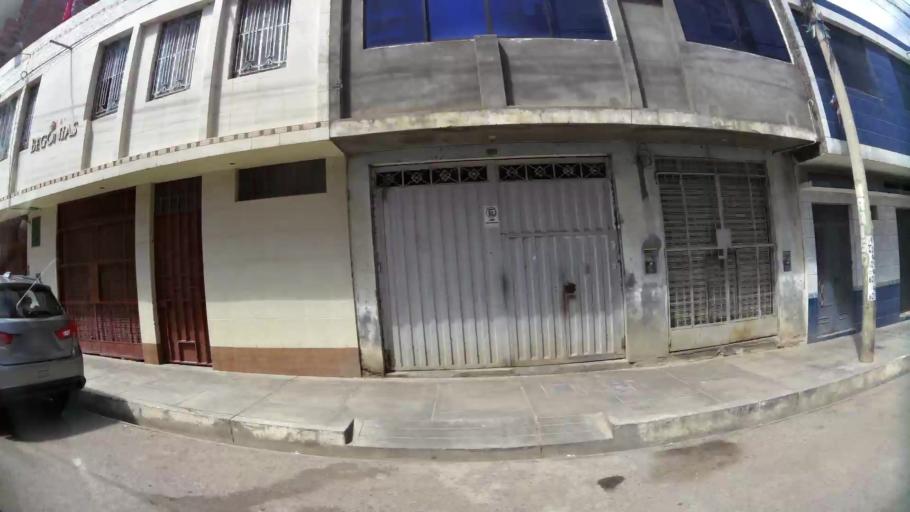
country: PE
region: Junin
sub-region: Provincia de Huancayo
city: El Tambo
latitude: -12.0738
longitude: -75.2141
